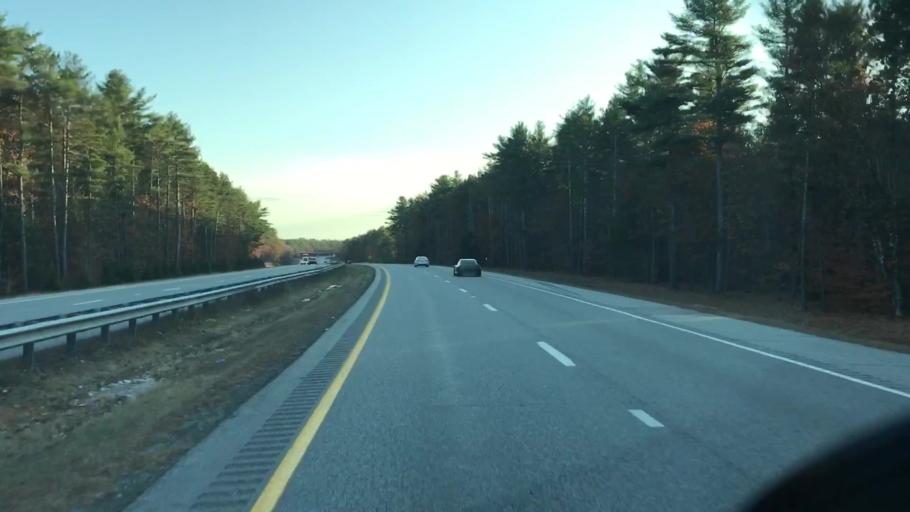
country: US
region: Maine
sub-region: Cumberland County
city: New Gloucester
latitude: 43.9964
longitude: -70.3090
